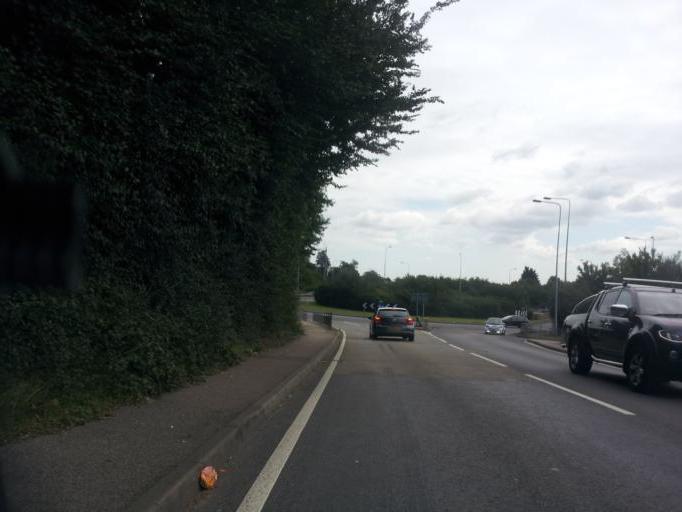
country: GB
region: England
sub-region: Kent
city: Newington
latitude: 51.3465
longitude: 0.6974
